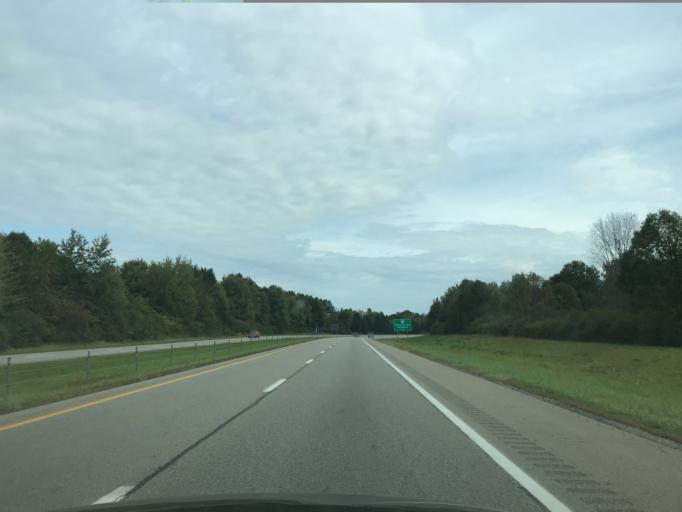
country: US
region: Ohio
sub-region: Trumbull County
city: Champion Heights
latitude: 41.2725
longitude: -80.8627
